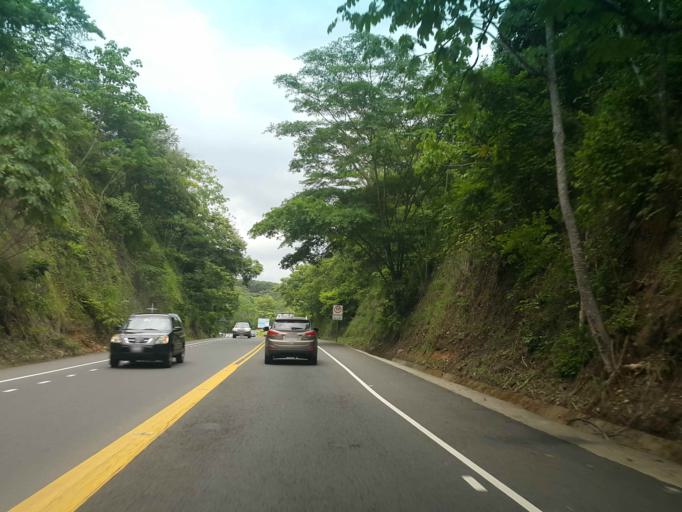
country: CR
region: Alajuela
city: Orotina
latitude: 9.8996
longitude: -84.5400
